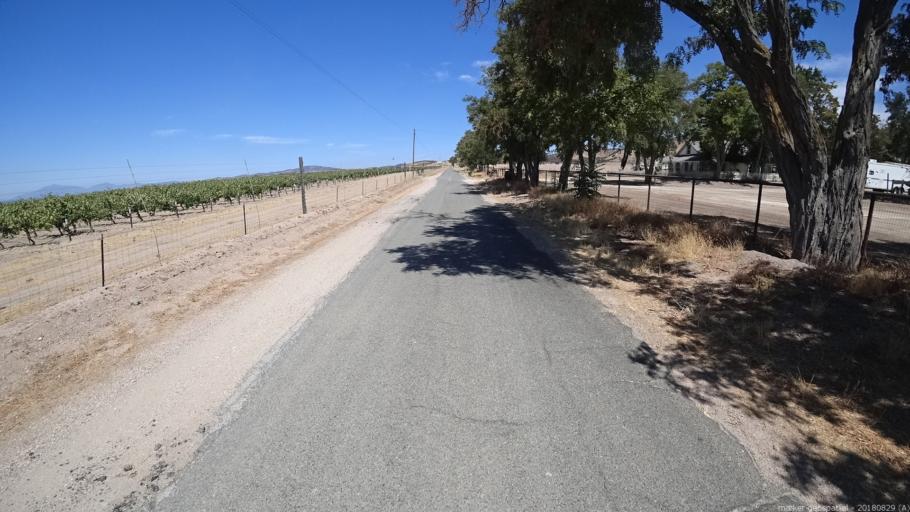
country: US
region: California
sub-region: San Luis Obispo County
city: Lake Nacimiento
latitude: 35.9157
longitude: -121.0379
